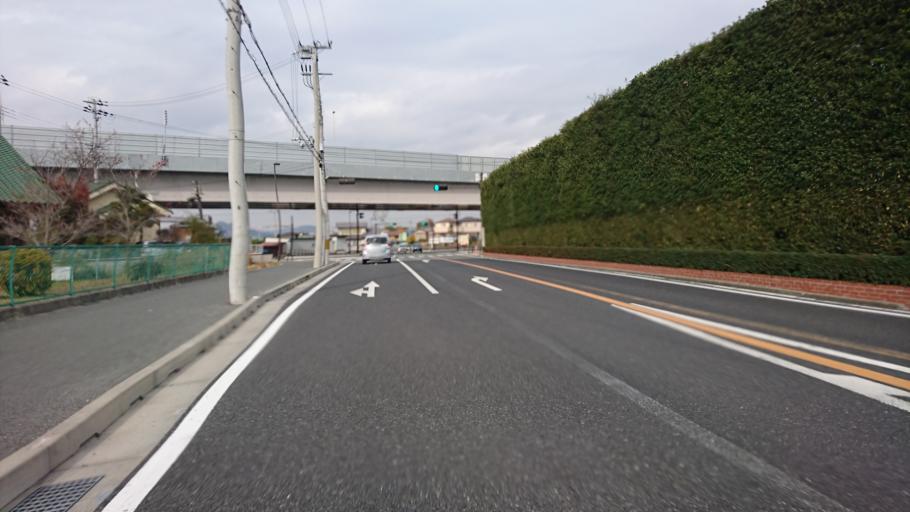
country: JP
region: Hyogo
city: Kakogawacho-honmachi
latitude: 34.7628
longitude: 134.8577
